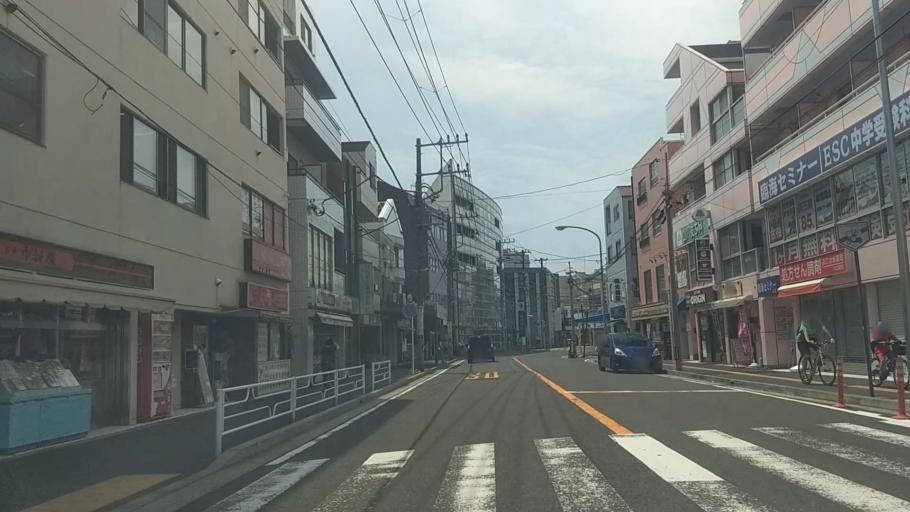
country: JP
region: Kanagawa
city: Yokohama
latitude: 35.4920
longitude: 139.6455
